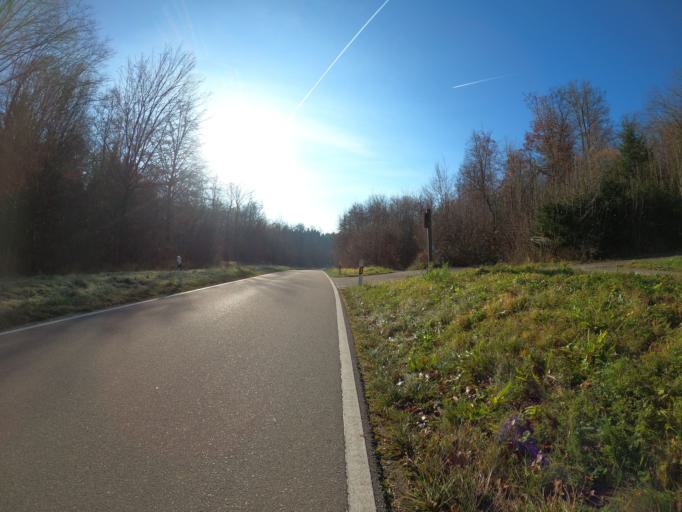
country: DE
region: Baden-Wuerttemberg
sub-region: Regierungsbezirk Stuttgart
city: Ebersbach an der Fils
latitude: 48.6982
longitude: 9.5390
